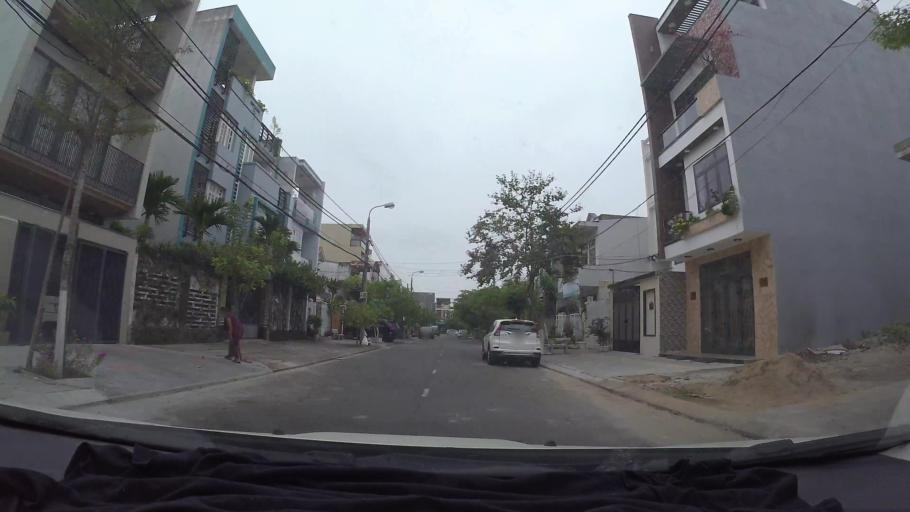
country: VN
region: Da Nang
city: Ngu Hanh Son
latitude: 16.0312
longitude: 108.2310
